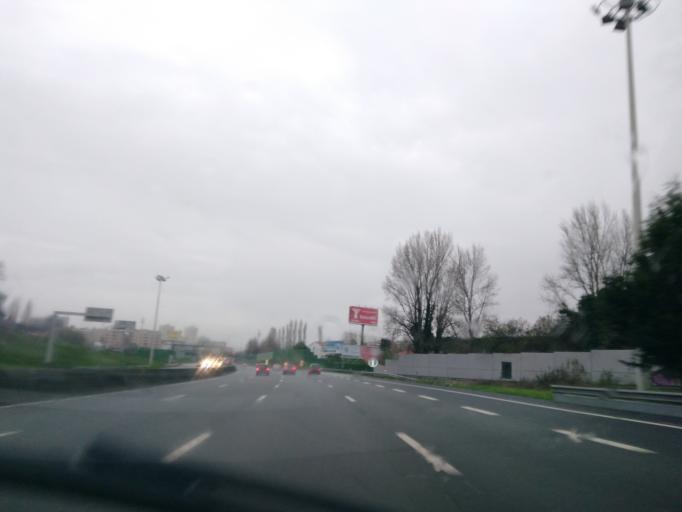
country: PT
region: Porto
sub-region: Maia
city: Pedroucos
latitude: 41.1814
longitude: -8.5929
